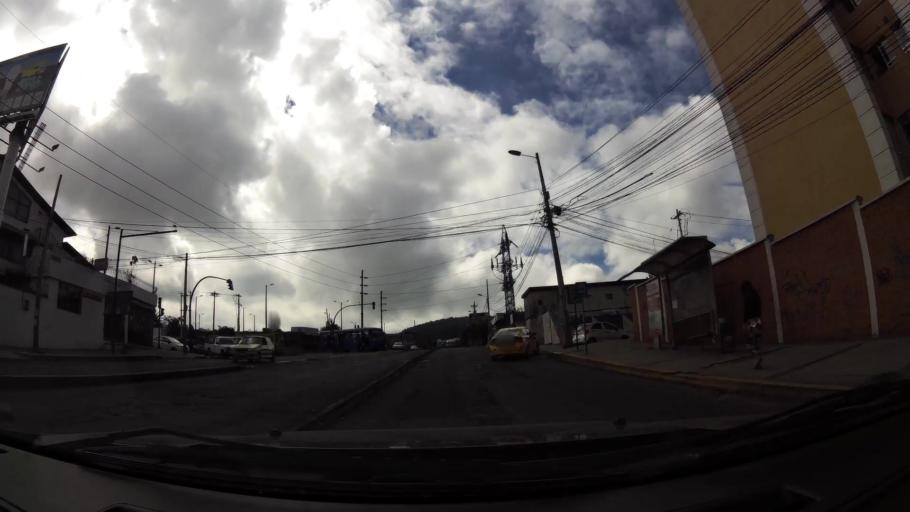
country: EC
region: Pichincha
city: Quito
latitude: -0.1636
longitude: -78.4745
